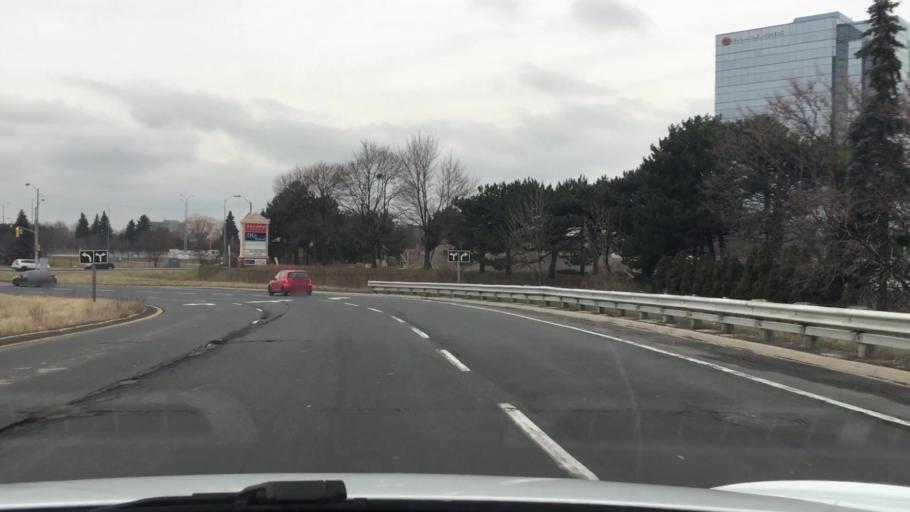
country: CA
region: Ontario
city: Scarborough
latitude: 43.7765
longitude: -79.2836
